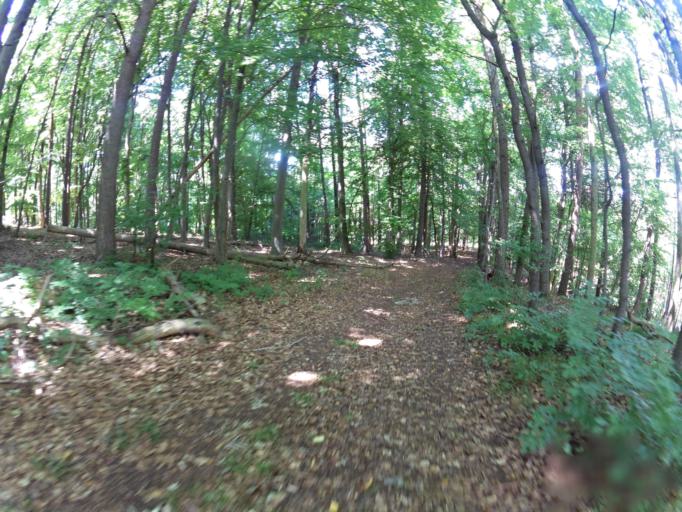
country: DE
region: Bavaria
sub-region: Regierungsbezirk Unterfranken
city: Thungersheim
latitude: 49.8967
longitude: 9.8514
